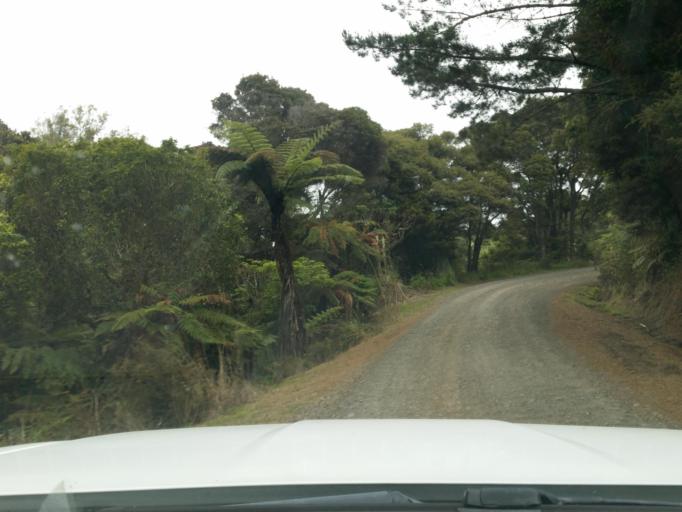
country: NZ
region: Northland
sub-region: Kaipara District
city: Dargaville
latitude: -35.7068
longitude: 173.6225
